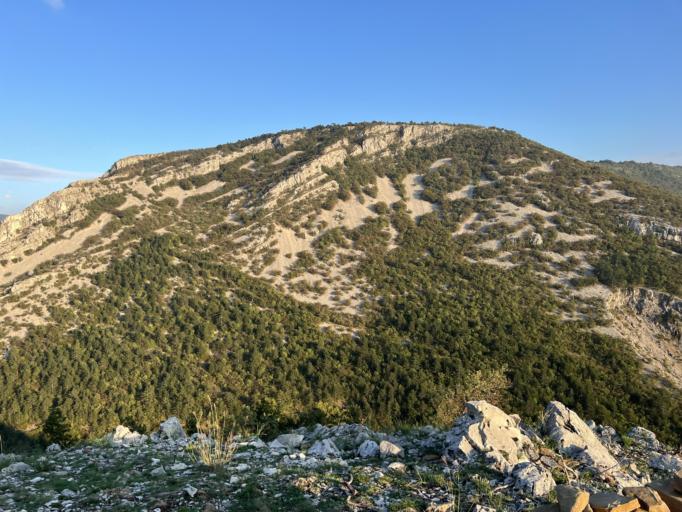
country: IT
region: Friuli Venezia Giulia
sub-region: Provincia di Trieste
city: Dolina
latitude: 45.6181
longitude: 13.8602
